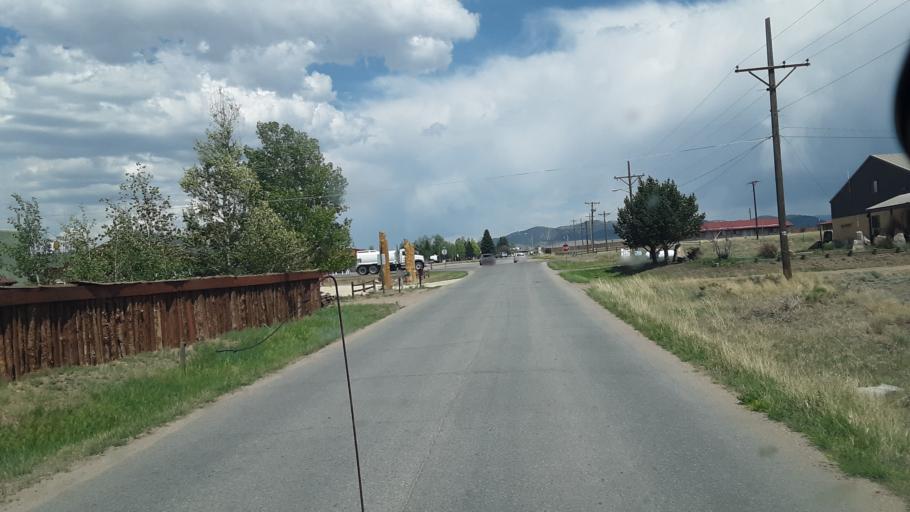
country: US
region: Colorado
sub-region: Custer County
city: Westcliffe
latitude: 38.1309
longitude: -105.4649
